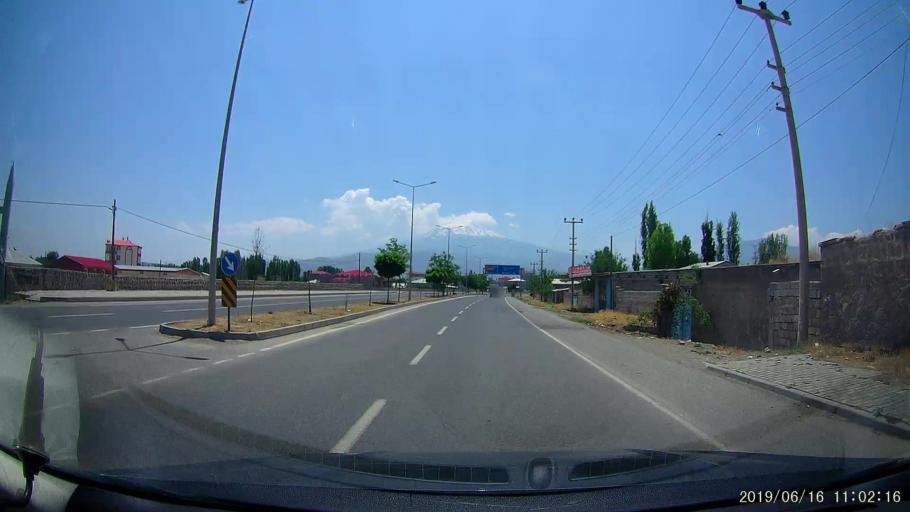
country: TR
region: Igdir
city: Igdir
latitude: 39.9081
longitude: 44.0581
